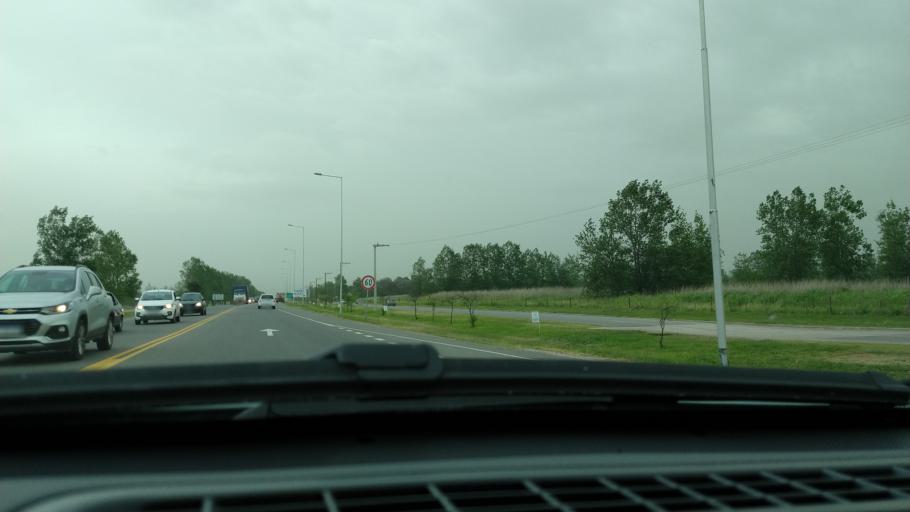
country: AR
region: Cordoba
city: Villa Allende
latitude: -31.3038
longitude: -64.2273
